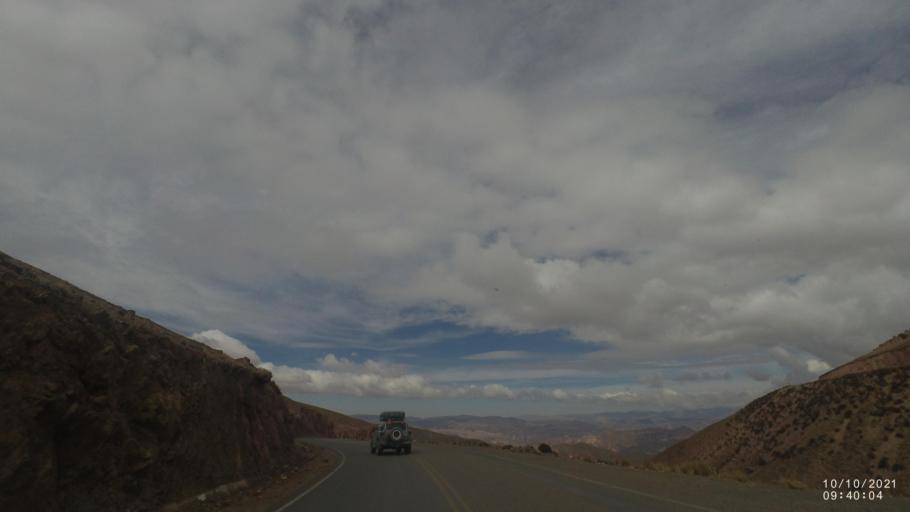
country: BO
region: La Paz
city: Quime
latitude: -17.1372
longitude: -67.3393
